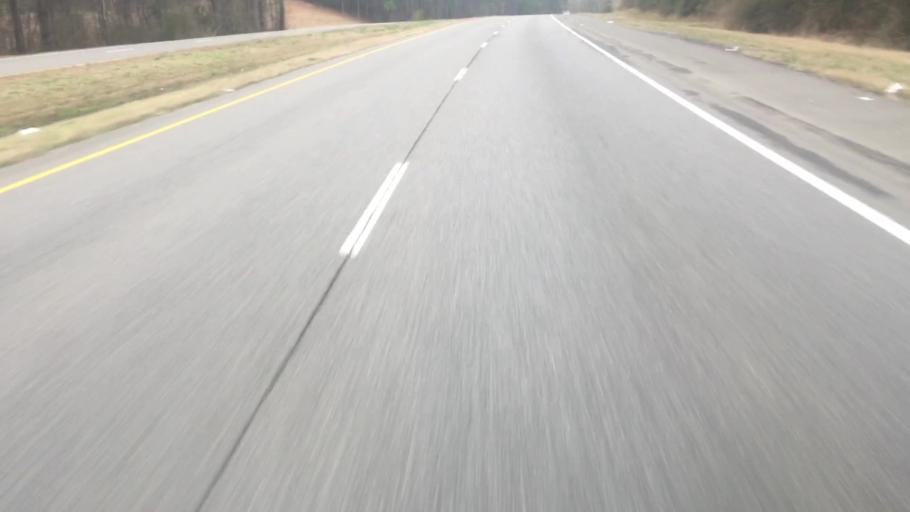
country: US
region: Alabama
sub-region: Jefferson County
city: Graysville
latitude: 33.6872
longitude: -86.9764
